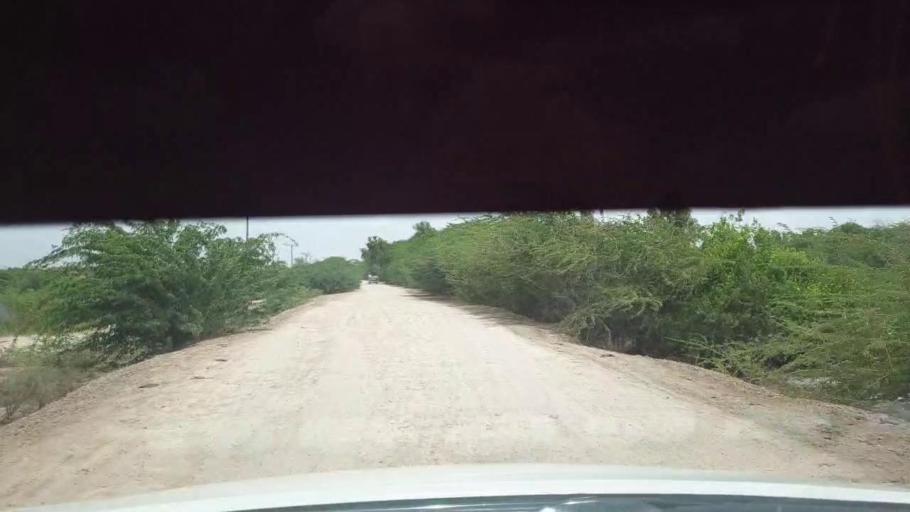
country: PK
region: Sindh
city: Kadhan
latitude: 24.4651
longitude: 69.0068
